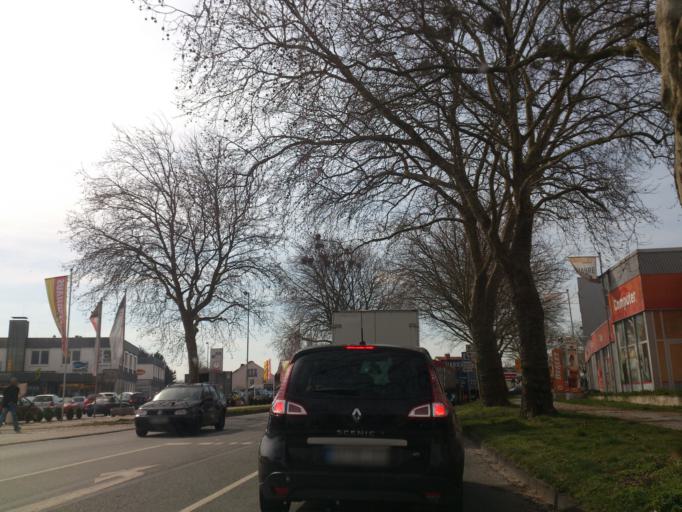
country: DE
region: North Rhine-Westphalia
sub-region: Regierungsbezirk Arnsberg
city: Soest
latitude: 51.5685
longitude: 8.1291
